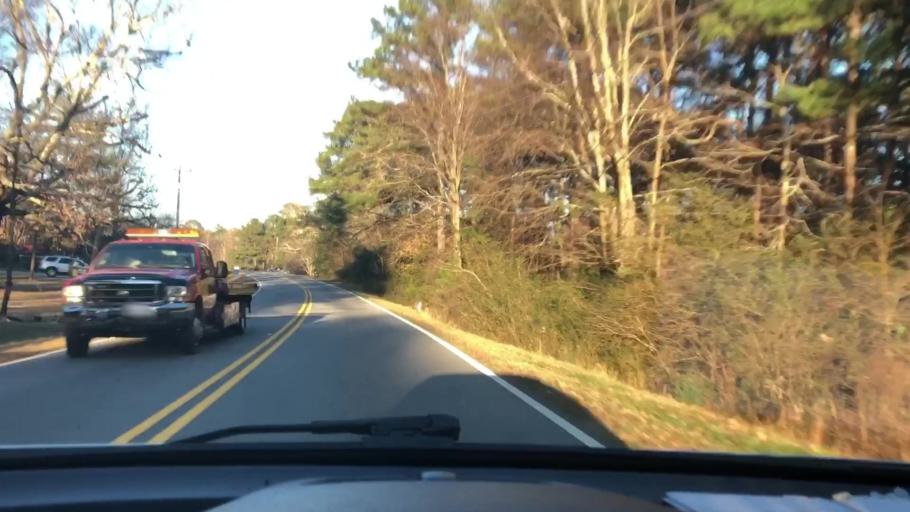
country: US
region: Georgia
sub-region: Rockdale County
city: Lakeview Estates
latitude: 33.7502
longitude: -84.0230
